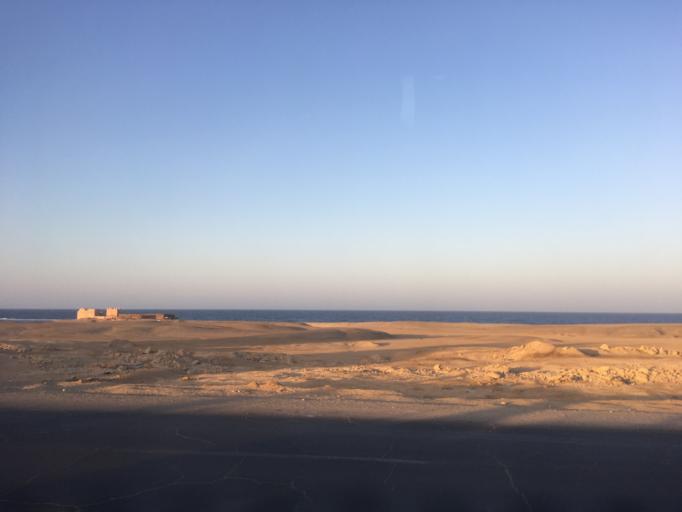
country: EG
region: Red Sea
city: Al Qusayr
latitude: 26.1495
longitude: 34.2504
